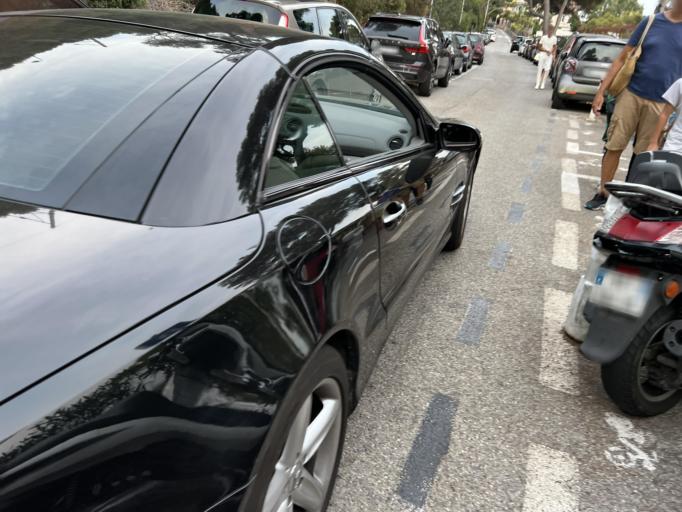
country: FR
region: Provence-Alpes-Cote d'Azur
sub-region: Departement des Alpes-Maritimes
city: Cap-d'Ail
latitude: 43.7203
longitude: 7.3942
